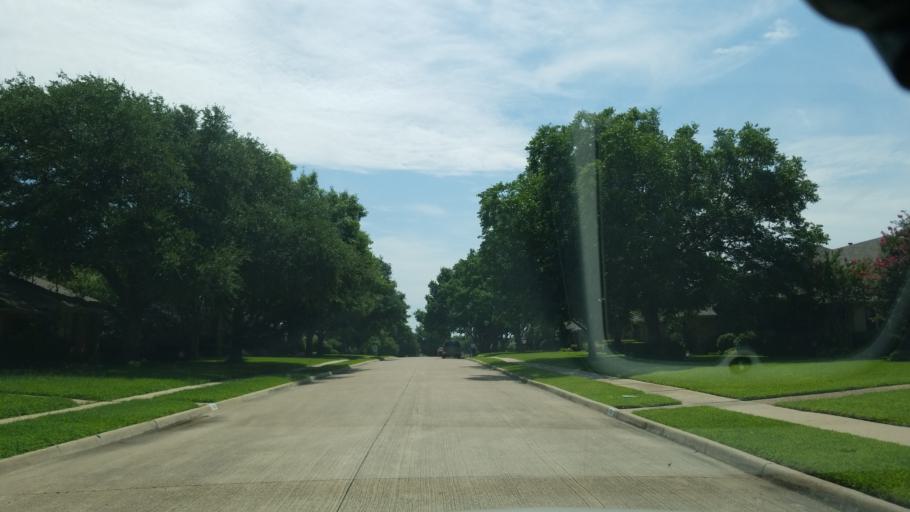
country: US
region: Texas
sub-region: Dallas County
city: Coppell
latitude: 32.9680
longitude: -96.9726
